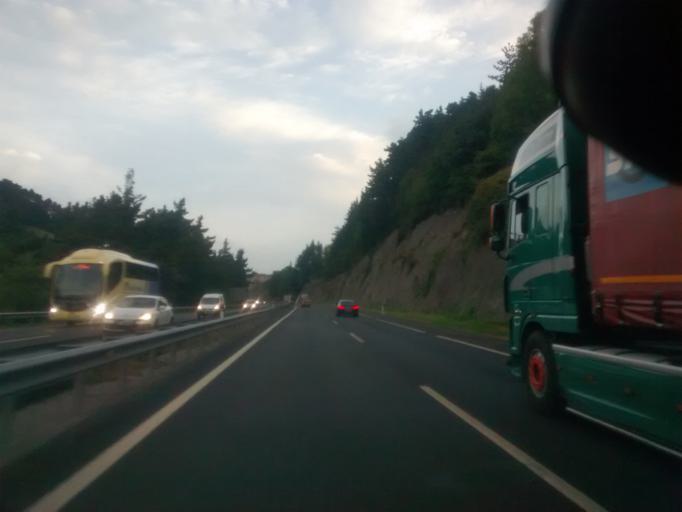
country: ES
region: Basque Country
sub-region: Provincia de Guipuzcoa
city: Deba
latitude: 43.2743
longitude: -2.3095
